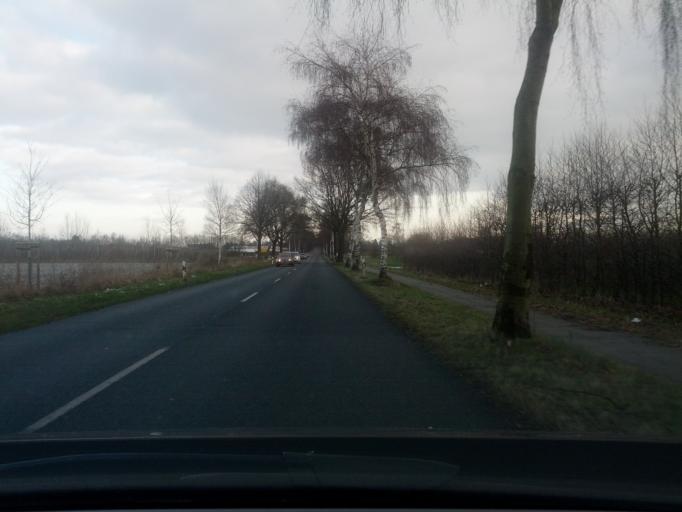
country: DE
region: Lower Saxony
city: Apensen
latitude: 53.4474
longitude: 9.6386
